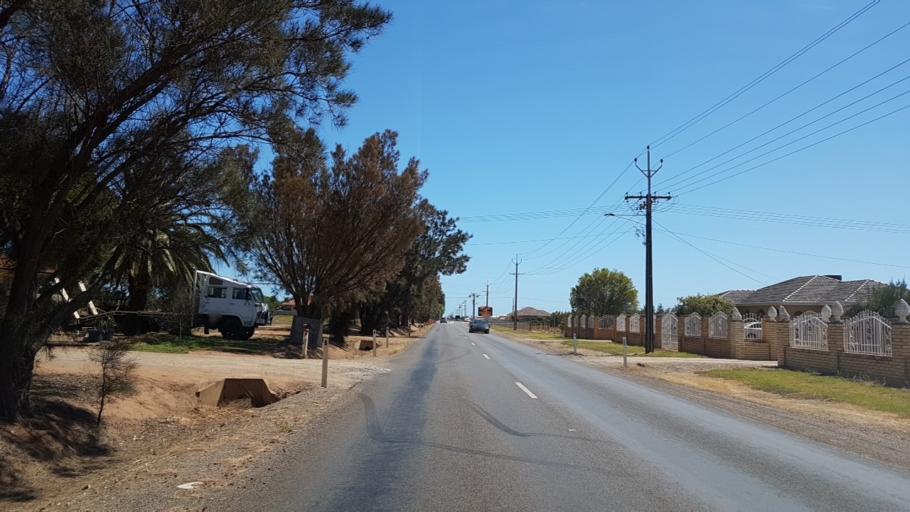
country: AU
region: South Australia
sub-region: Playford
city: Virginia
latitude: -34.7269
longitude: 138.5708
